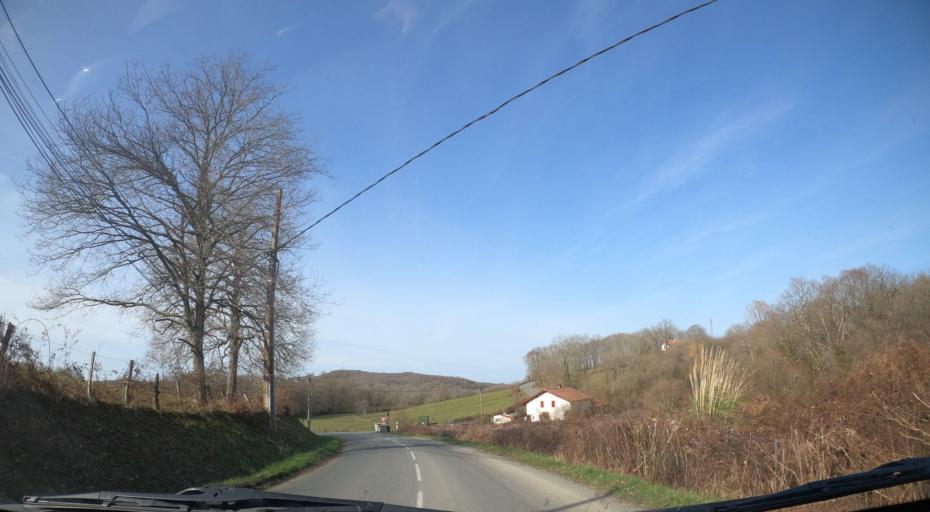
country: FR
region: Aquitaine
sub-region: Departement des Pyrenees-Atlantiques
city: Lahonce
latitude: 43.4527
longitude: -1.3710
